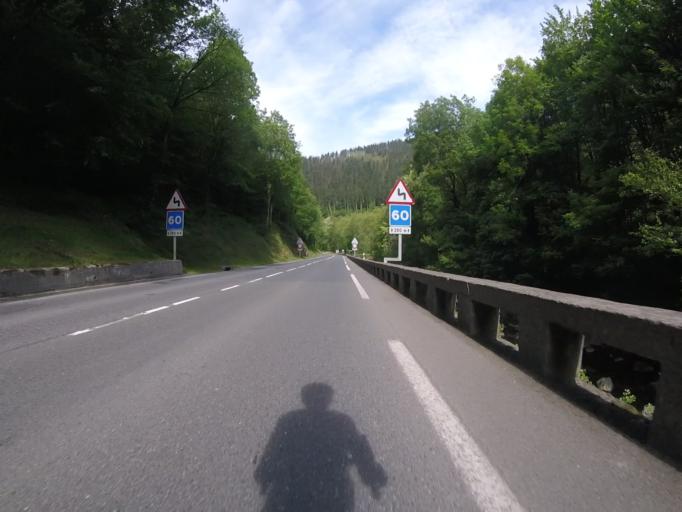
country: ES
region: Basque Country
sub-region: Provincia de Guipuzcoa
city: Urretxu
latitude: 43.1139
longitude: -2.3289
